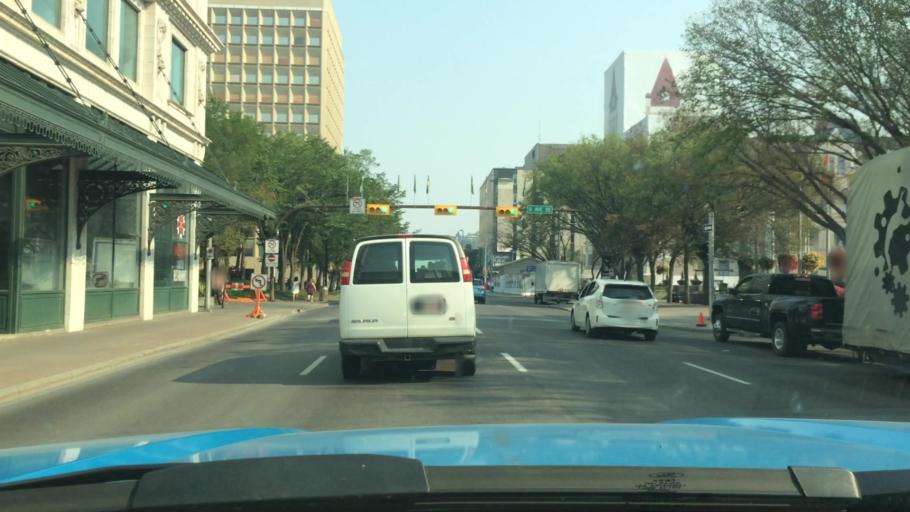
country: CA
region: Alberta
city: Calgary
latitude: 51.0450
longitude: -114.0582
